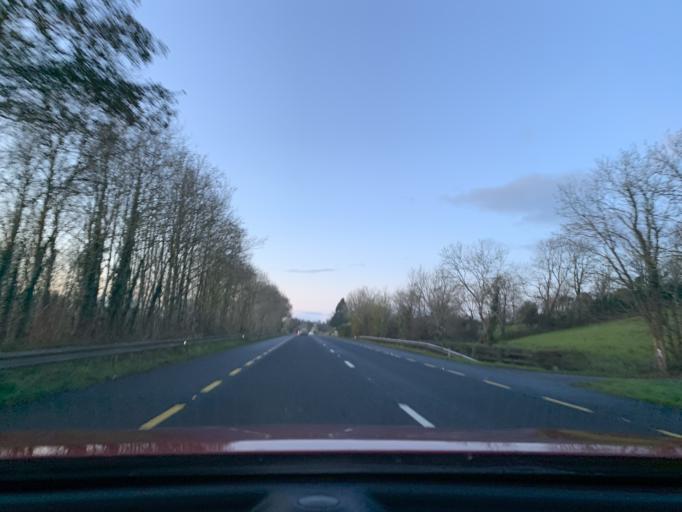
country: IE
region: Connaught
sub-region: County Leitrim
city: Carrick-on-Shannon
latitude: 53.9086
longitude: -7.9637
